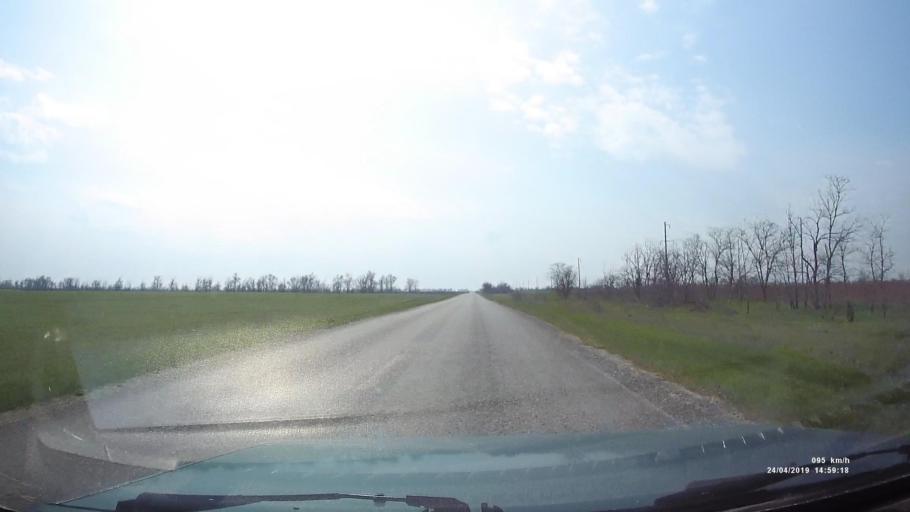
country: RU
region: Rostov
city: Remontnoye
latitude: 46.5663
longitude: 43.5806
